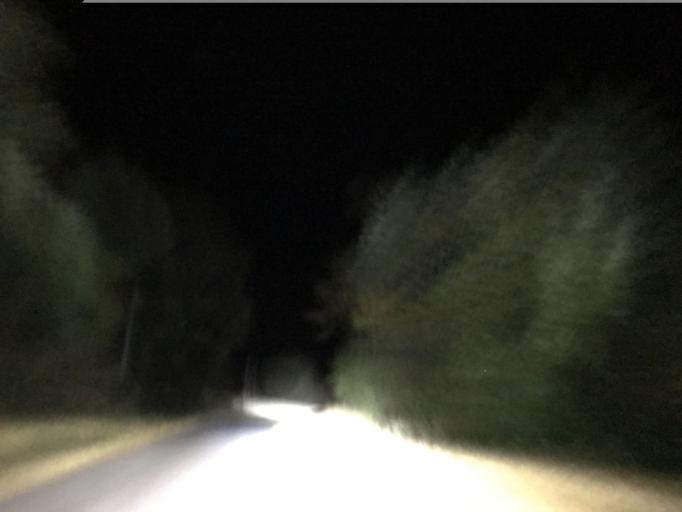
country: FR
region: Auvergne
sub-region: Departement du Puy-de-Dome
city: La Monnerie-le-Montel
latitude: 45.8658
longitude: 3.6147
